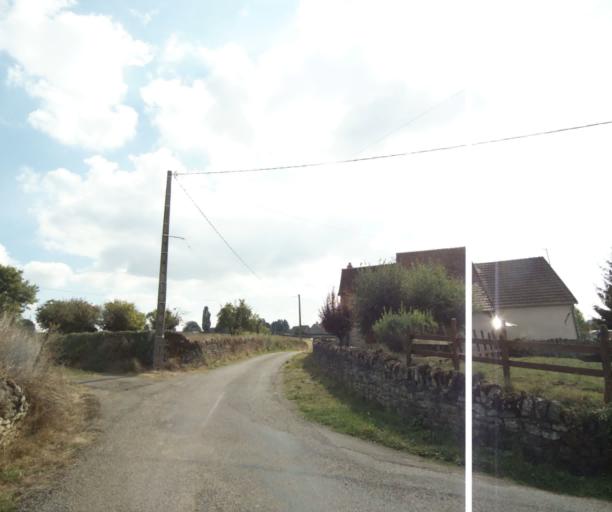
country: FR
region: Bourgogne
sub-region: Departement de Saone-et-Loire
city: Charolles
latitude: 46.3673
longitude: 4.2463
